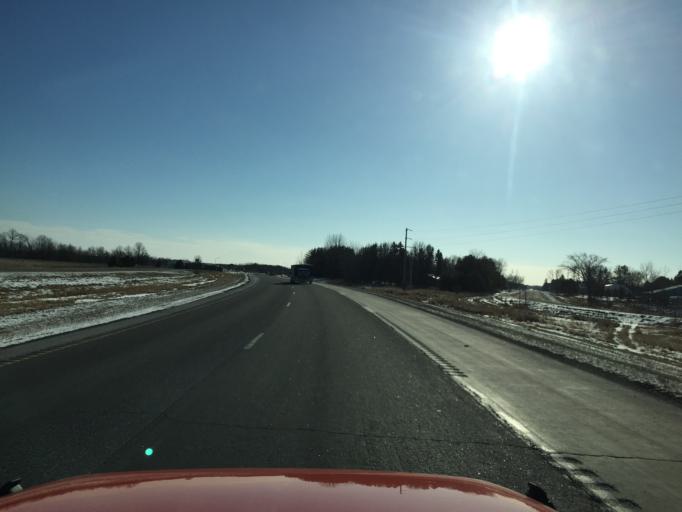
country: US
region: Minnesota
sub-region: Mille Lacs County
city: Milaca
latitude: 45.7886
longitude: -93.6540
